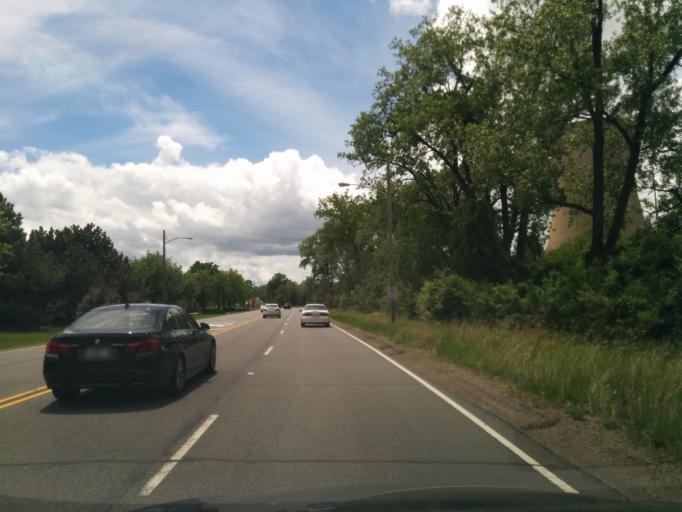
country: US
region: Indiana
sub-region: LaPorte County
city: Michigan City
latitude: 41.7177
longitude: -86.9091
